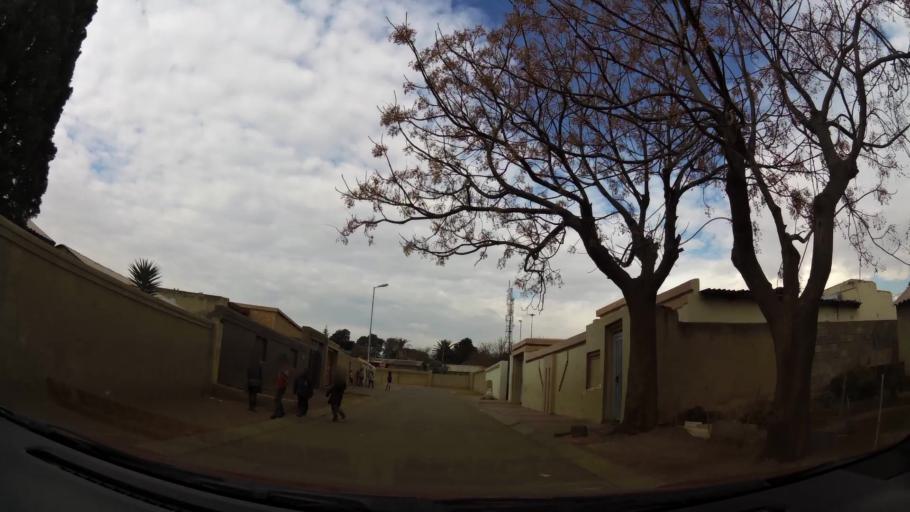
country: ZA
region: Gauteng
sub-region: City of Johannesburg Metropolitan Municipality
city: Soweto
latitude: -26.2448
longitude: 27.8540
